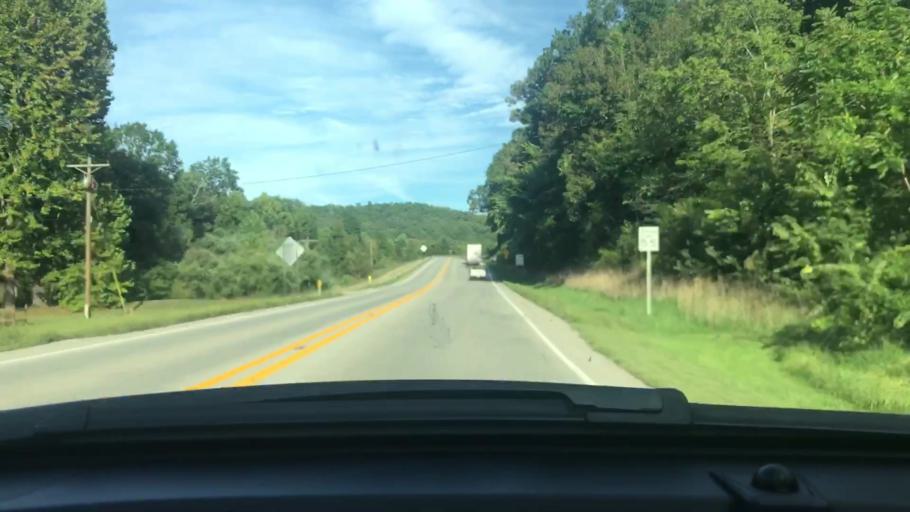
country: US
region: Arkansas
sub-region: Sharp County
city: Cherokee Village
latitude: 36.3038
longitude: -91.4215
